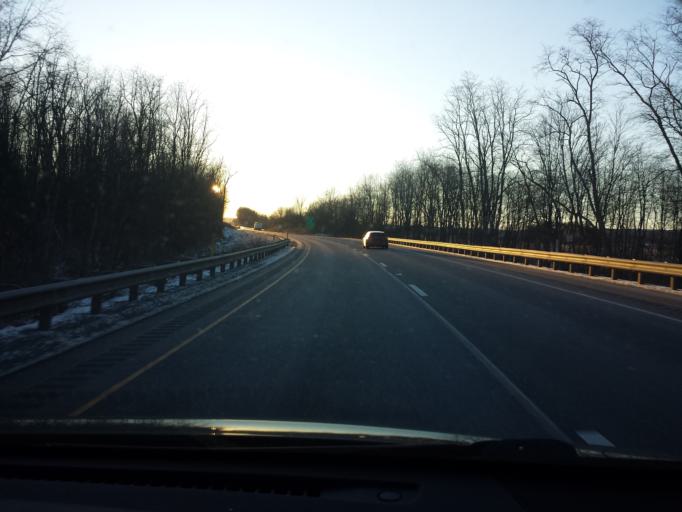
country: US
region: Pennsylvania
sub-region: Clinton County
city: Mill Hall
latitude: 41.0402
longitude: -77.4931
